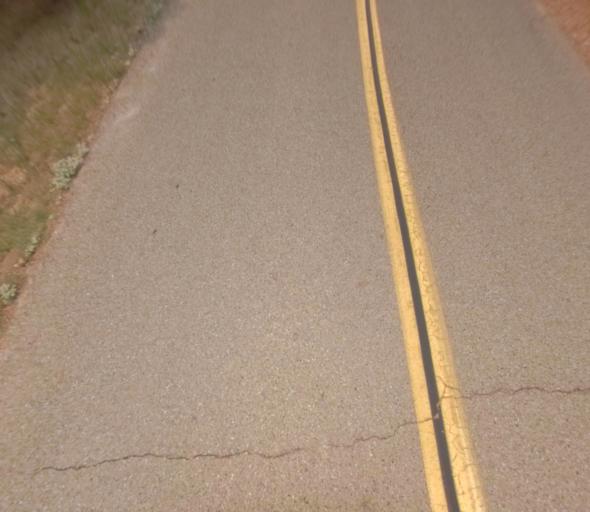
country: US
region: California
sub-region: Madera County
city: Oakhurst
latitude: 37.3369
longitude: -119.6050
